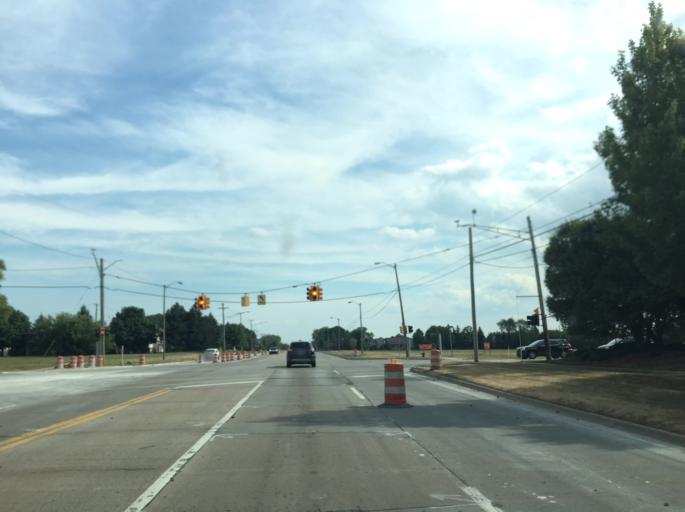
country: US
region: Michigan
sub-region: Macomb County
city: Fraser
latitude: 42.5477
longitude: -82.9896
